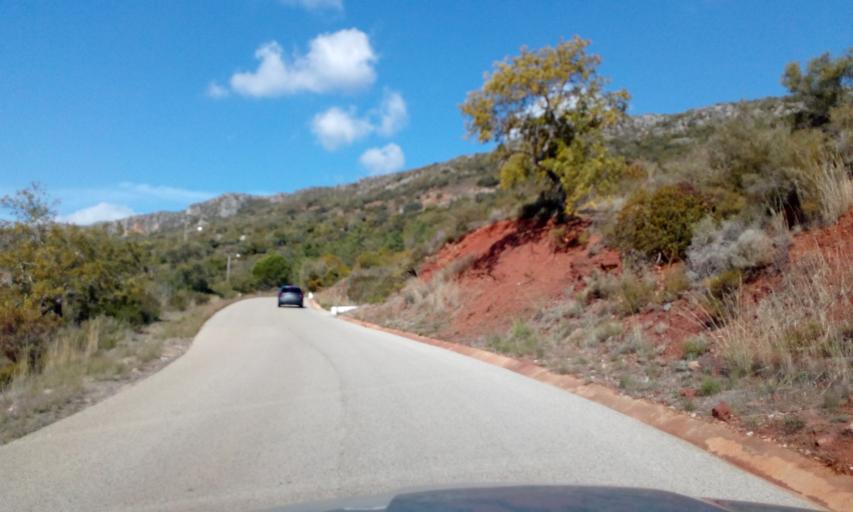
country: PT
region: Faro
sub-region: Loule
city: Boliqueime
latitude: 37.2486
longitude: -8.0910
